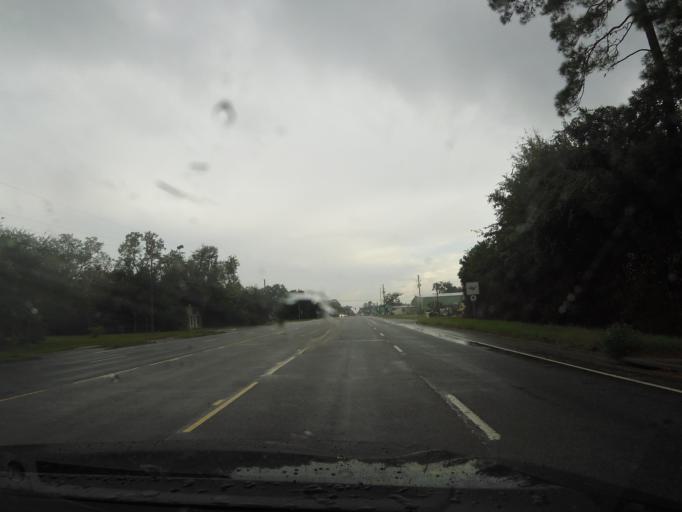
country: US
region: Georgia
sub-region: Wayne County
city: Jesup
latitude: 31.5922
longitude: -81.8672
